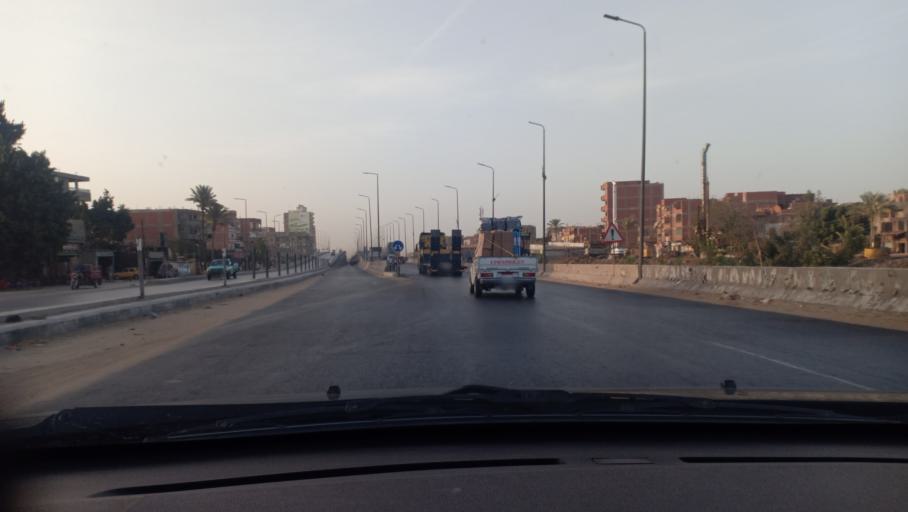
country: EG
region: Muhafazat al Minufiyah
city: Quwaysina
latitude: 30.5448
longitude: 31.2692
